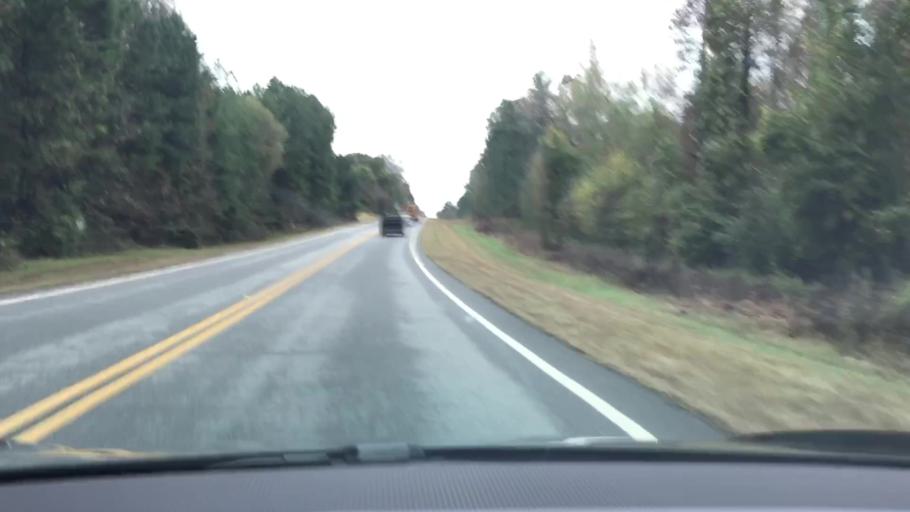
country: US
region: Georgia
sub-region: Greene County
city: Greensboro
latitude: 33.6349
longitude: -83.2173
